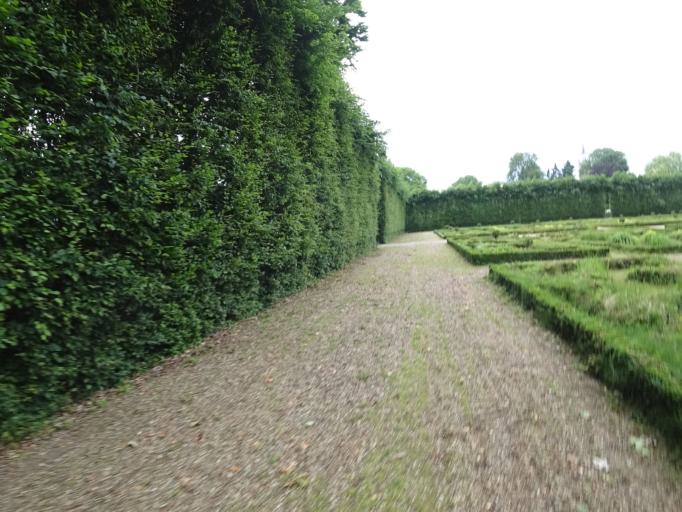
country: BE
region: Wallonia
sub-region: Province du Hainaut
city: Enghien
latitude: 50.6895
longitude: 4.0400
